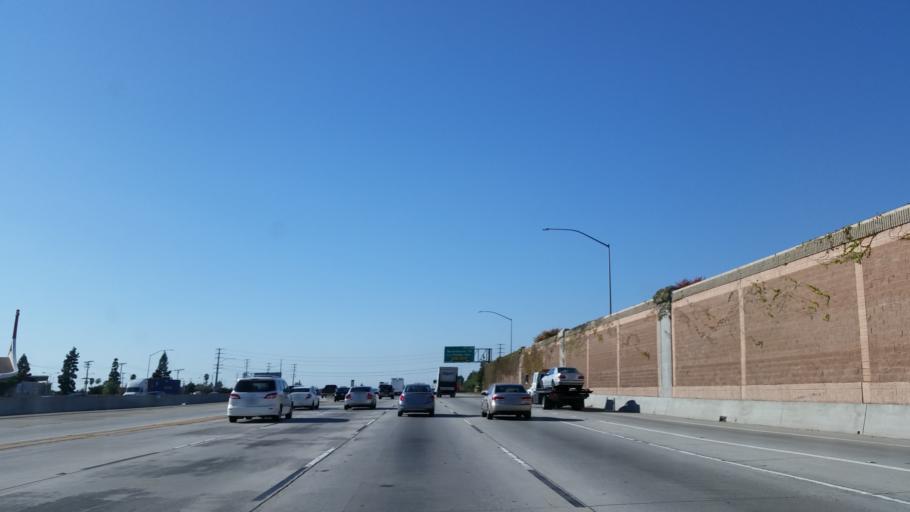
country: US
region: California
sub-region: Orange County
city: Anaheim
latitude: 33.8376
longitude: -117.9446
